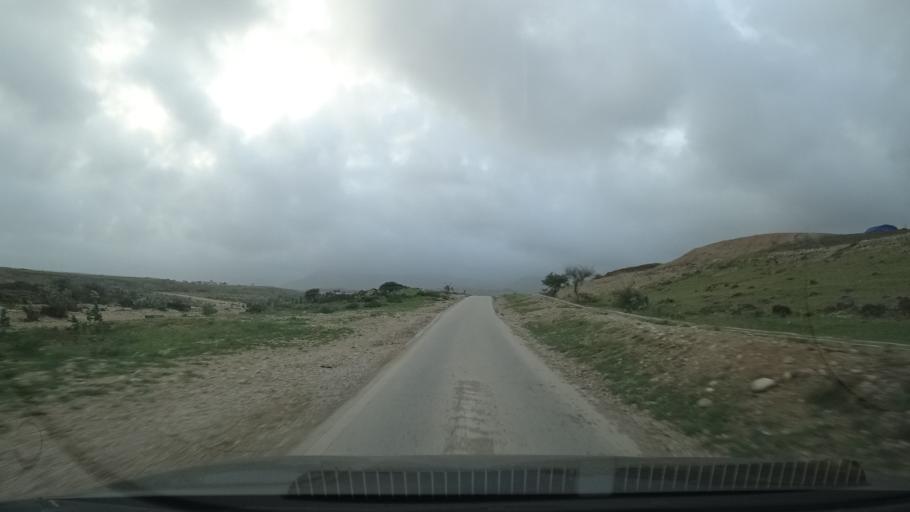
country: OM
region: Zufar
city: Salalah
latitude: 17.1069
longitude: 54.2297
